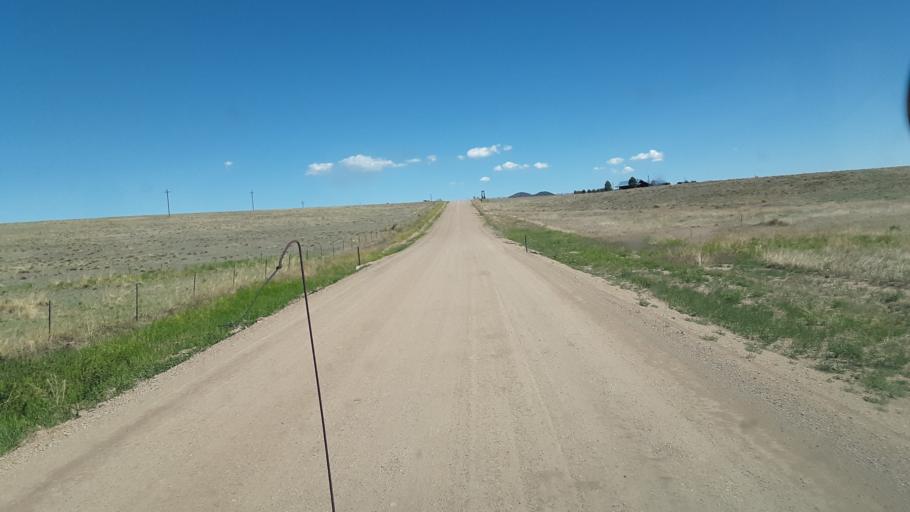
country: US
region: Colorado
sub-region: Custer County
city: Westcliffe
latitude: 38.2559
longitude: -105.4995
